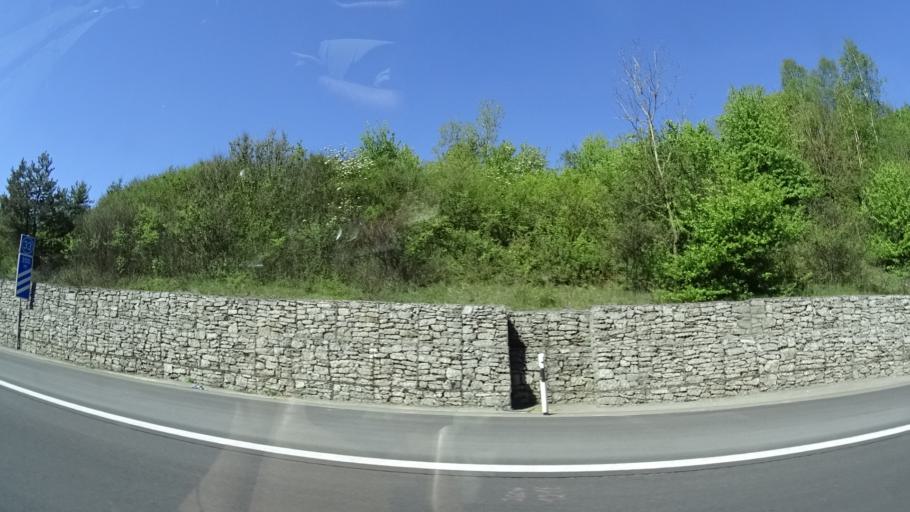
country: DE
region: Baden-Wuerttemberg
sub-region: Freiburg Region
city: Vohringen
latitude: 48.3029
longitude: 8.6352
